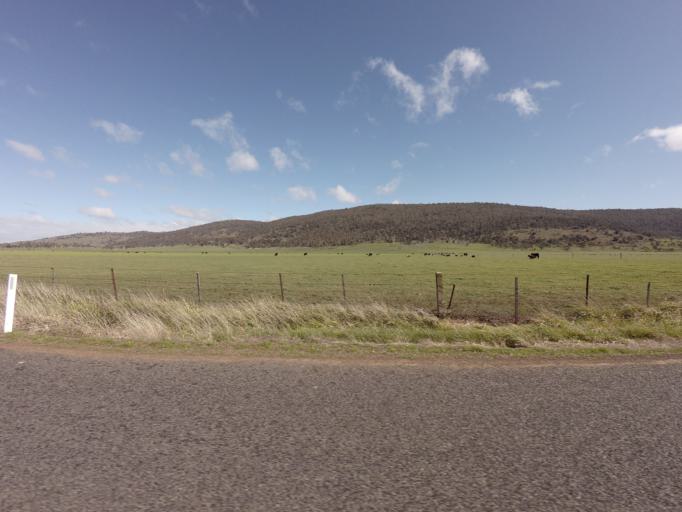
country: AU
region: Tasmania
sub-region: Northern Midlands
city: Evandale
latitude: -41.9744
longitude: 147.4450
